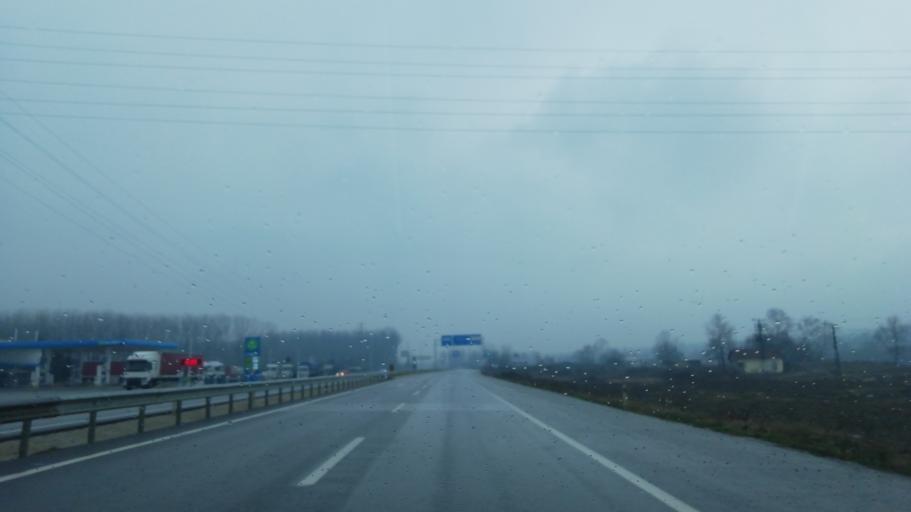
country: TR
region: Sakarya
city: Akyazi
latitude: 40.6622
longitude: 30.5958
